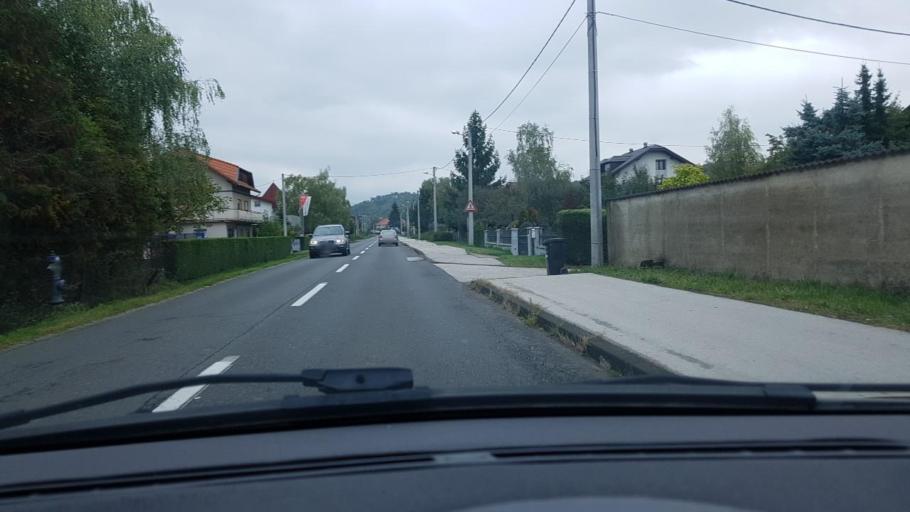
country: HR
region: Grad Zagreb
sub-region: Sesvete
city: Sesvete
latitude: 45.8739
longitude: 16.1136
